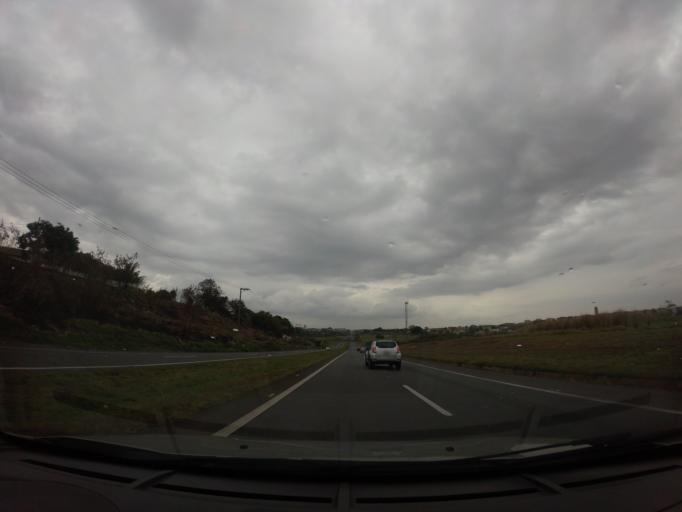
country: BR
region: Sao Paulo
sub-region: Santa Barbara D'Oeste
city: Santa Barbara d'Oeste
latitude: -22.7670
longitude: -47.4262
